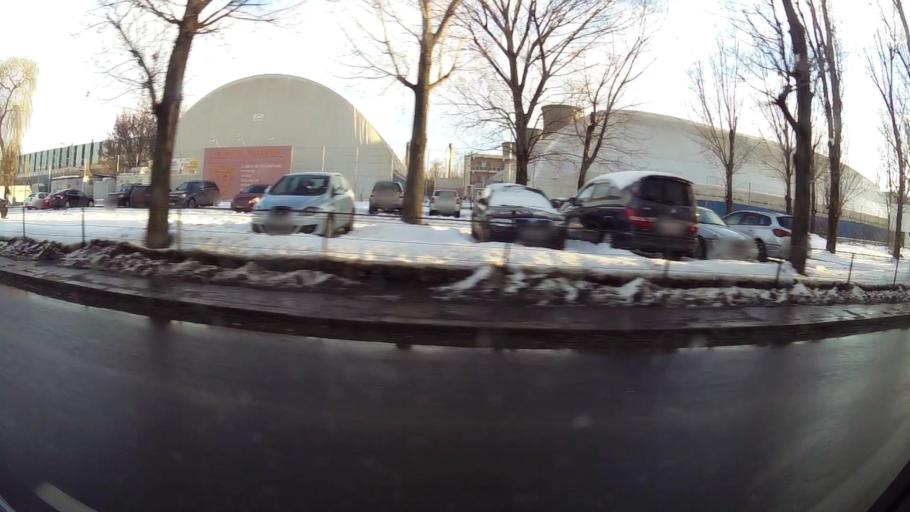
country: RO
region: Ilfov
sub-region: Comuna Popesti-Leordeni
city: Popesti-Leordeni
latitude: 44.3676
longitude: 26.1339
